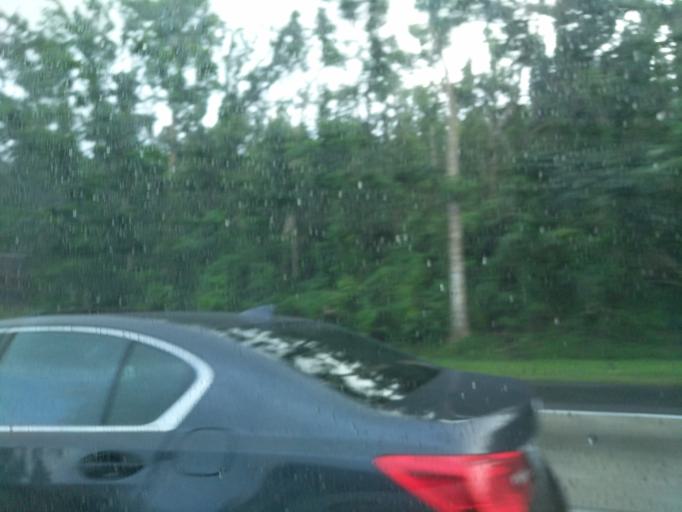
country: PR
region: Cidra
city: Bayamon
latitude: 18.1715
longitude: -66.0733
